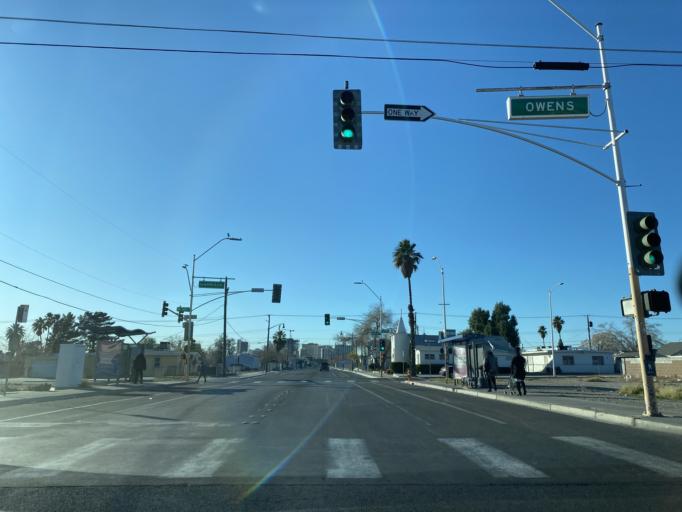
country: US
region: Nevada
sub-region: Clark County
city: Las Vegas
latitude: 36.1885
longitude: -115.1473
